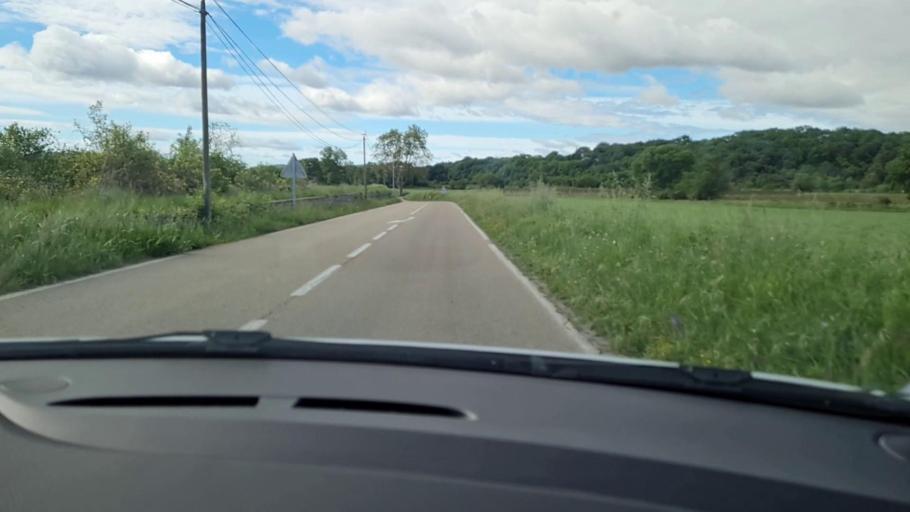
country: FR
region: Languedoc-Roussillon
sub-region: Departement du Gard
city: Quissac
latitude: 43.9019
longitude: 4.0011
